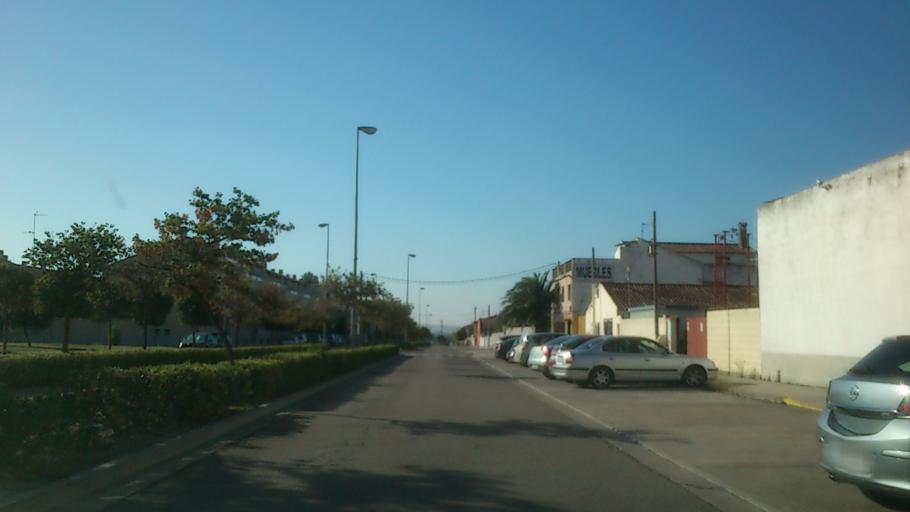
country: ES
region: Aragon
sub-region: Provincia de Zaragoza
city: Villanueva de Gallego
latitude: 41.7756
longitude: -0.8265
